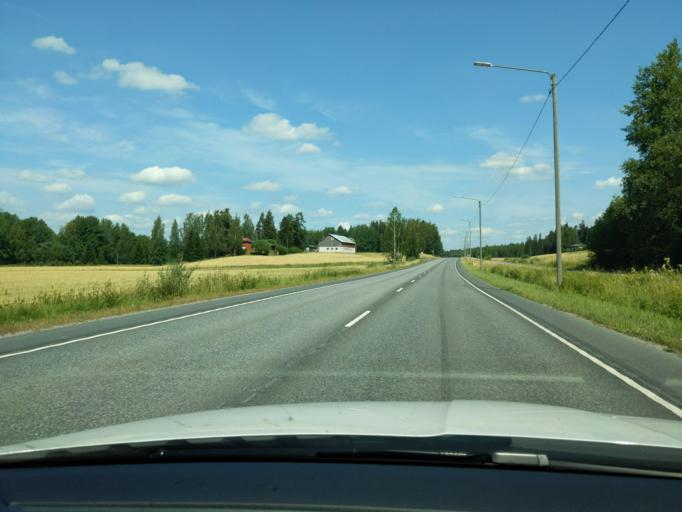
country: FI
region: Uusimaa
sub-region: Helsinki
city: Kerava
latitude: 60.3774
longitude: 25.1269
